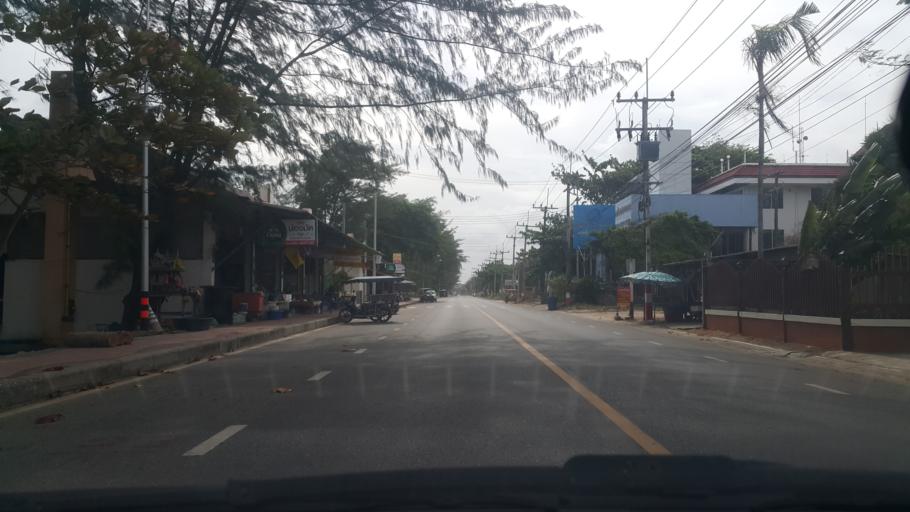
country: TH
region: Rayong
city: Rayong
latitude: 12.6184
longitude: 101.3719
